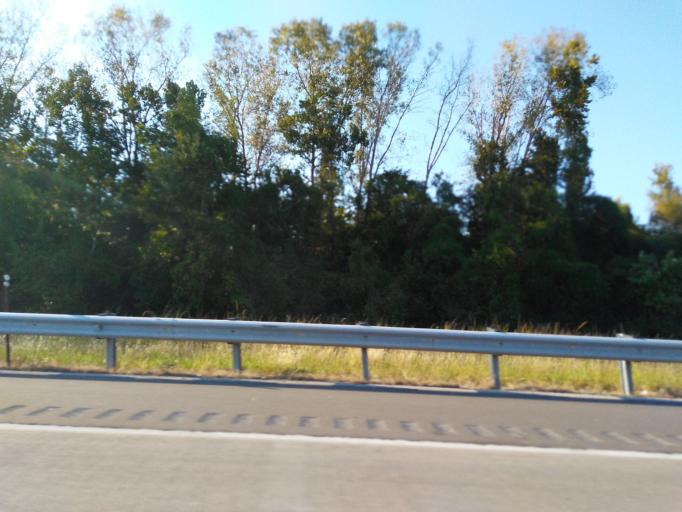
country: US
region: Illinois
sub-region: Saint Clair County
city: Washington Park
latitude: 38.6334
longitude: -90.0630
